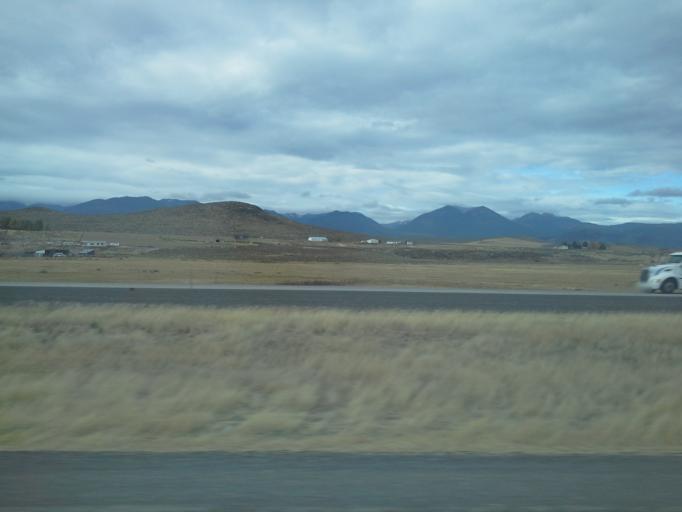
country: US
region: Oregon
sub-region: Baker County
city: Baker City
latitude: 44.9874
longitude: -117.8951
